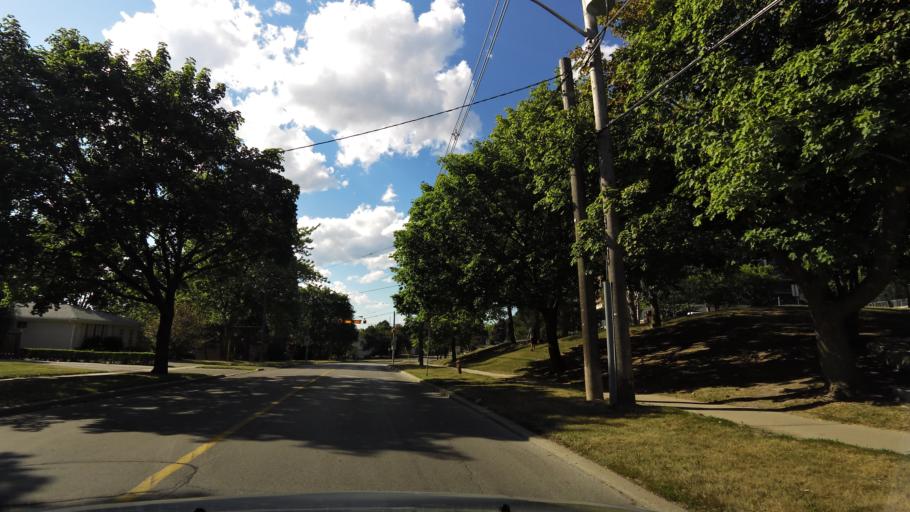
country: CA
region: Ontario
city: Willowdale
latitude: 43.7807
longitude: -79.3546
